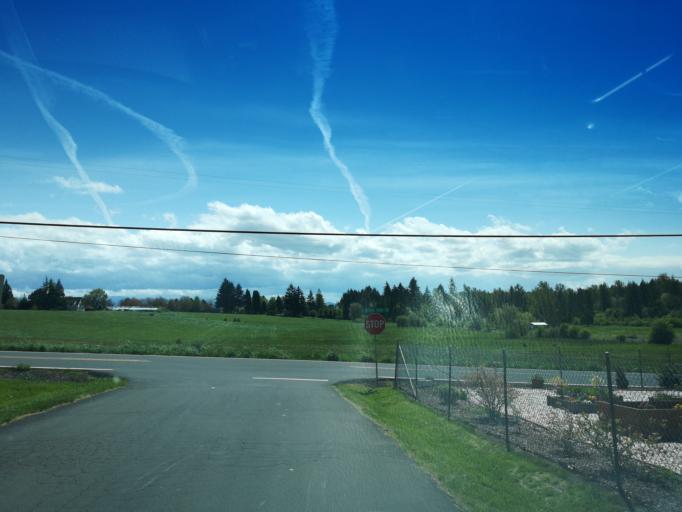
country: US
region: Oregon
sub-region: Clackamas County
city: Damascus
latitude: 45.4328
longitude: -122.4178
